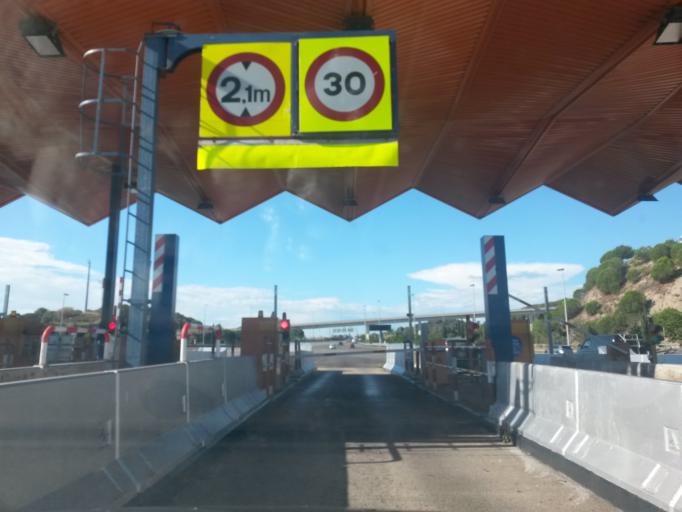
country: ES
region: Catalonia
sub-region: Provincia de Barcelona
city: Arenys de Mar
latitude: 41.5877
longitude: 2.5385
